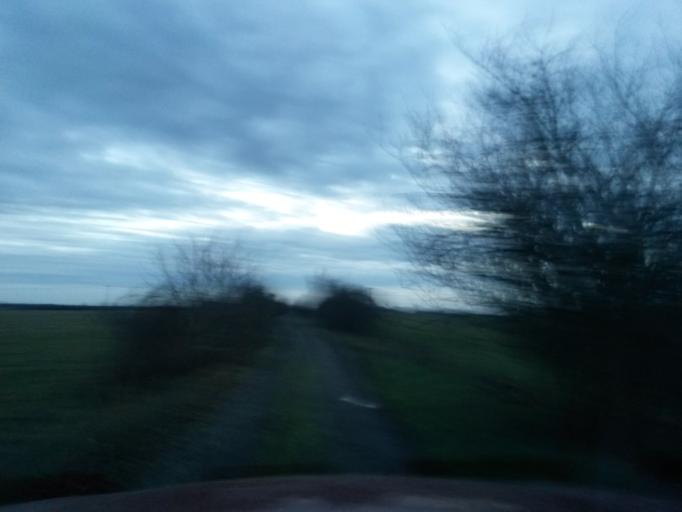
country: HU
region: Borsod-Abauj-Zemplen
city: Karcsa
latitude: 48.4345
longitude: 21.8681
